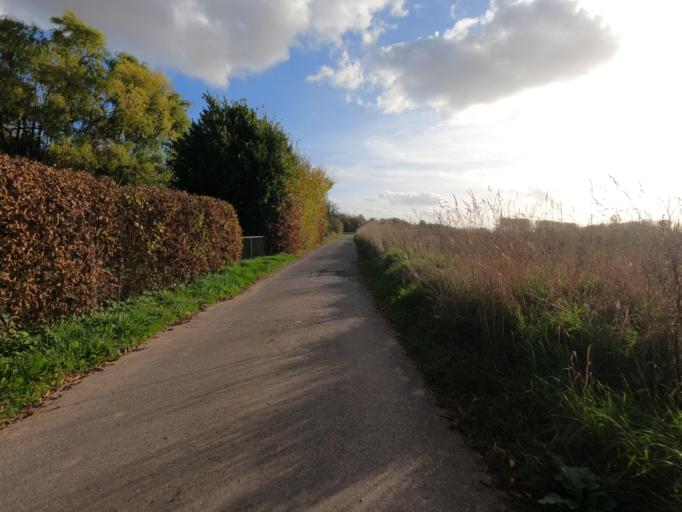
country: DE
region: North Rhine-Westphalia
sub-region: Regierungsbezirk Koln
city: Titz
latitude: 51.0837
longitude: 6.4069
